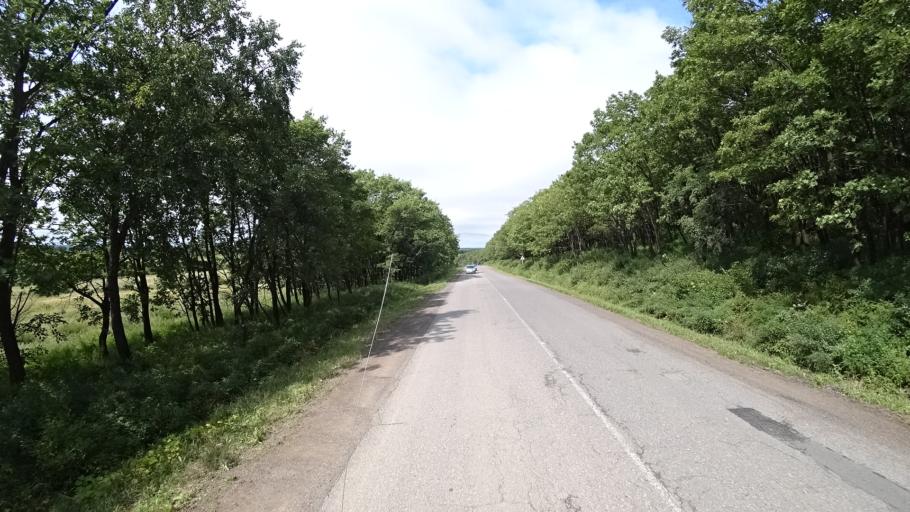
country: RU
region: Primorskiy
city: Lyalichi
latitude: 44.1505
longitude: 132.3933
